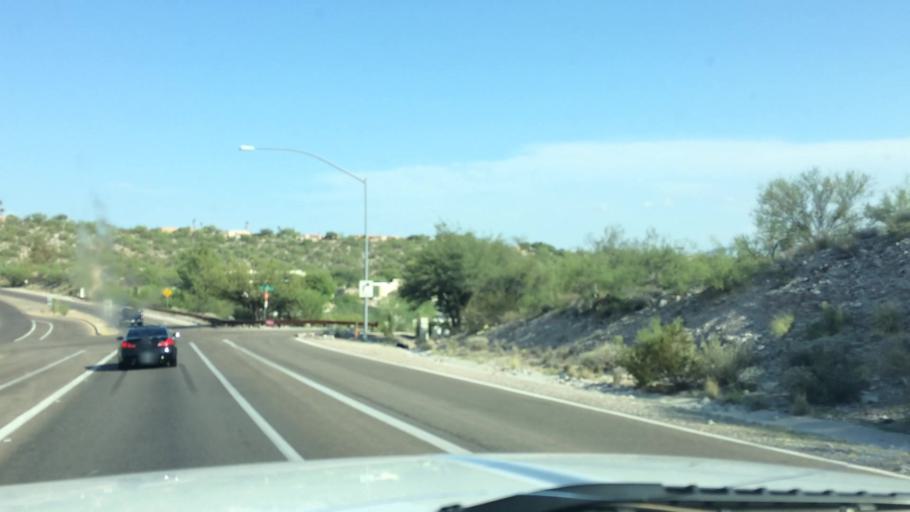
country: US
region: Arizona
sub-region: Pima County
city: Catalina Foothills
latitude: 32.3071
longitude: -110.8704
